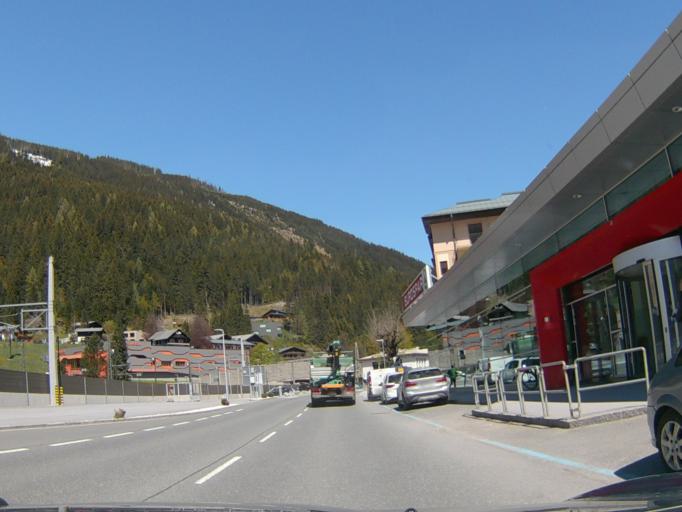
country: AT
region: Salzburg
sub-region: Politischer Bezirk Sankt Johann im Pongau
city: Bad Gastein
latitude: 47.1096
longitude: 13.1335
